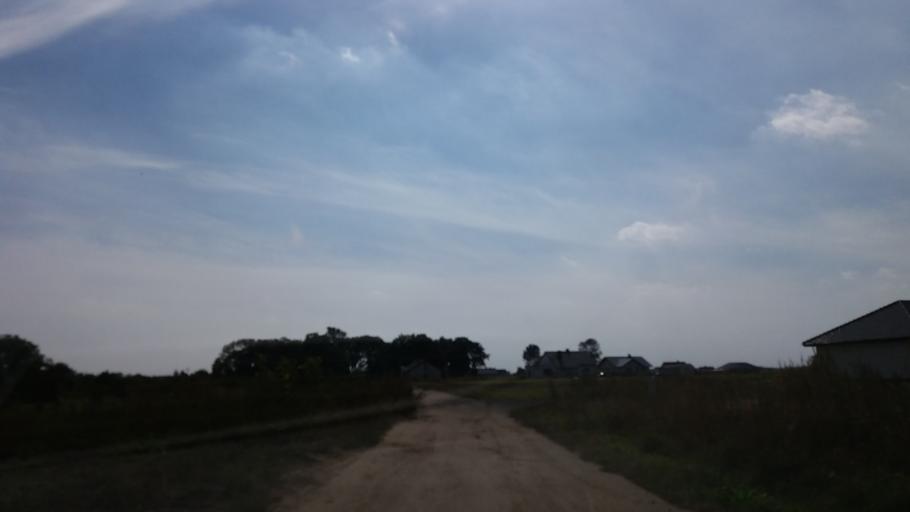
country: PL
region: West Pomeranian Voivodeship
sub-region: Powiat stargardzki
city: Stargard Szczecinski
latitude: 53.3717
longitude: 14.9681
